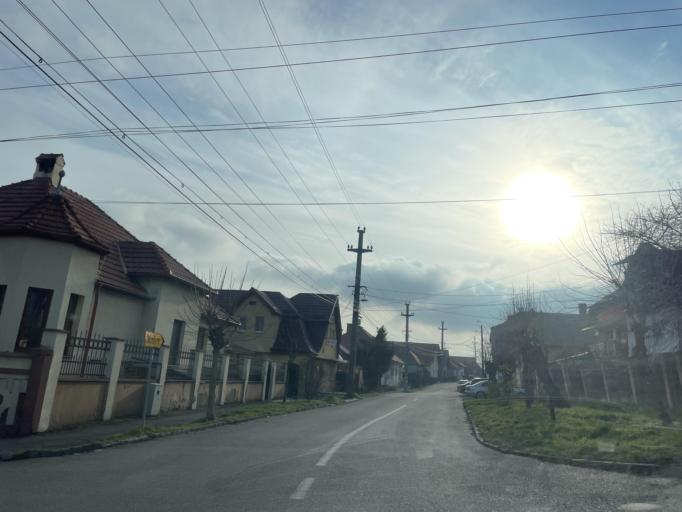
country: RO
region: Mures
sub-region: Municipiul Reghin
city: Reghin
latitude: 46.7820
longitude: 24.6943
